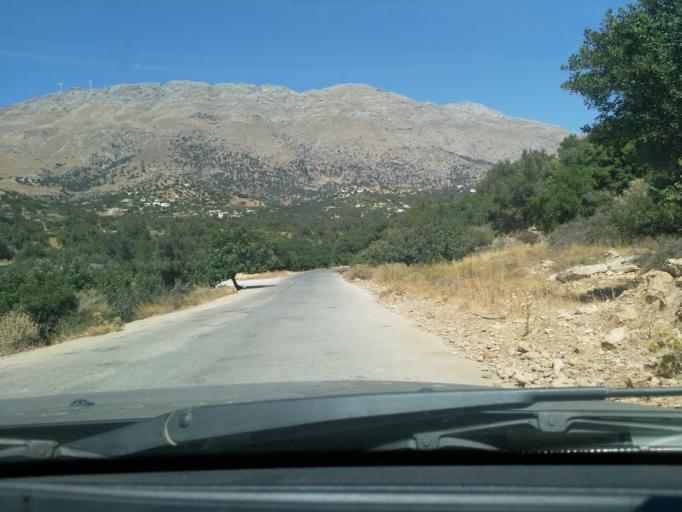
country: GR
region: Crete
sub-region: Nomos Rethymnis
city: Agia Galini
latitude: 35.1232
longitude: 24.5588
